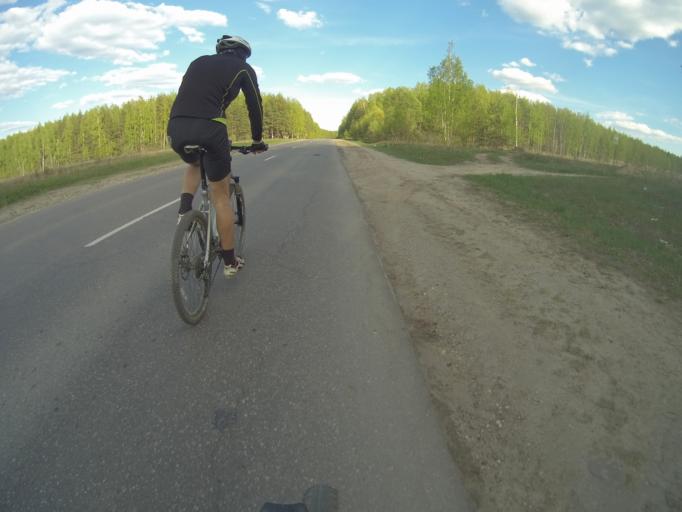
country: RU
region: Vladimir
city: Raduzhnyy
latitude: 55.9877
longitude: 40.2250
